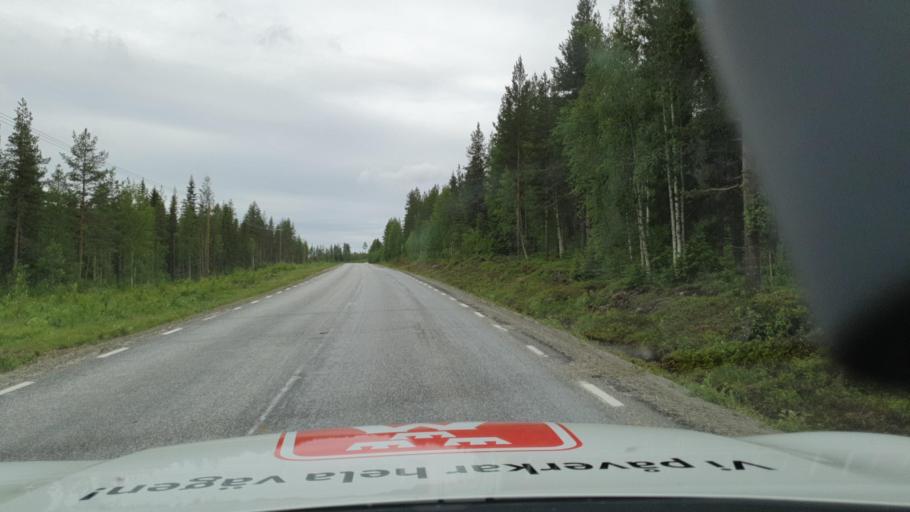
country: SE
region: Vaesterbotten
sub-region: Lycksele Kommun
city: Lycksele
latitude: 64.1488
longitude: 18.3599
